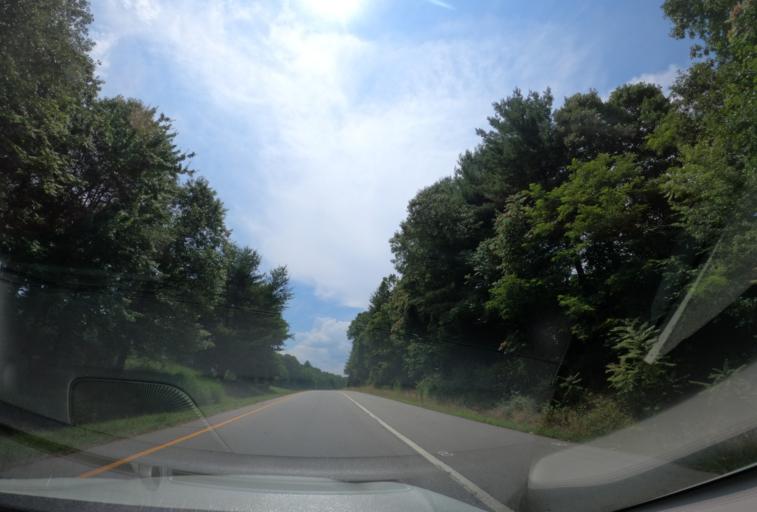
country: US
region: North Carolina
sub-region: Buncombe County
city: Biltmore Forest
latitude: 35.5600
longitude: -82.5426
